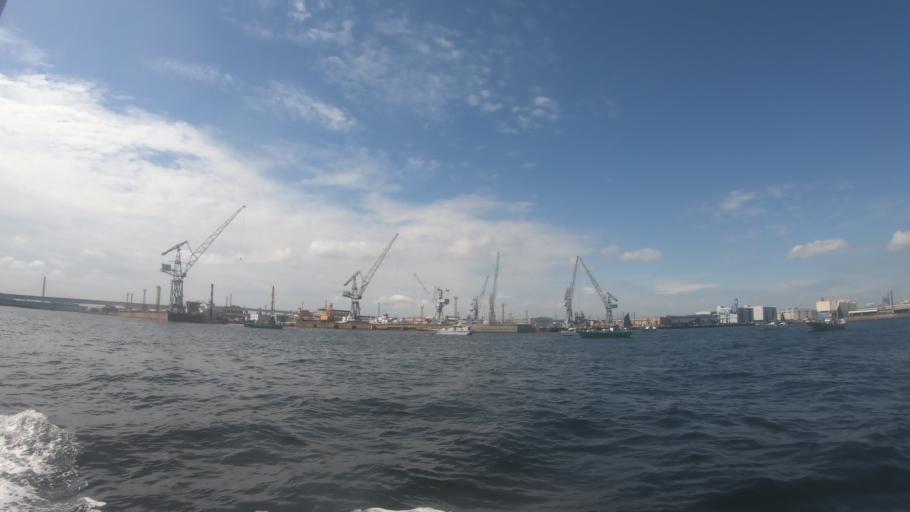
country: JP
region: Kanagawa
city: Yokohama
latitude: 35.4190
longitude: 139.6857
